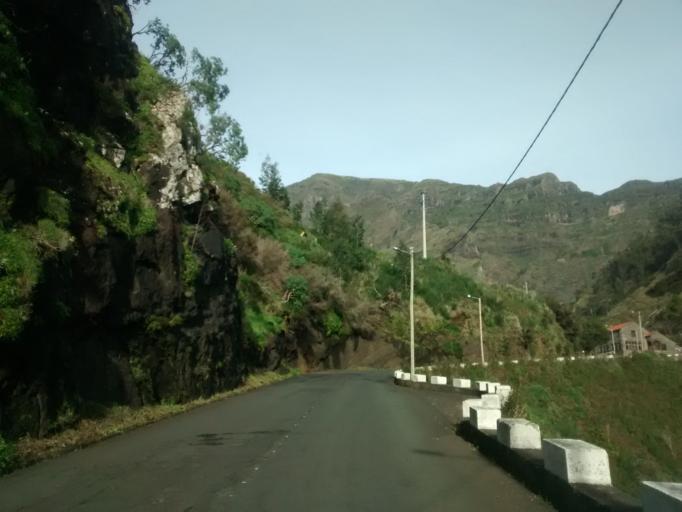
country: PT
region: Madeira
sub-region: Camara de Lobos
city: Curral das Freiras
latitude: 32.7349
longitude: -17.0245
